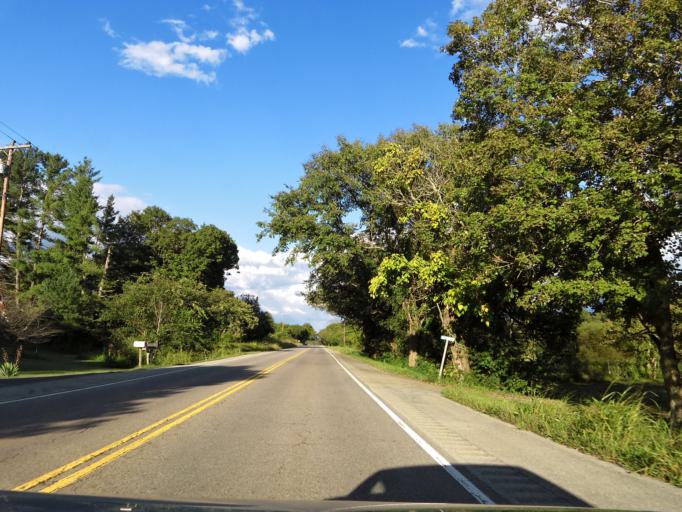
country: US
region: Tennessee
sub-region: Grainger County
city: Rutledge
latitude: 36.2621
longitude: -83.5679
